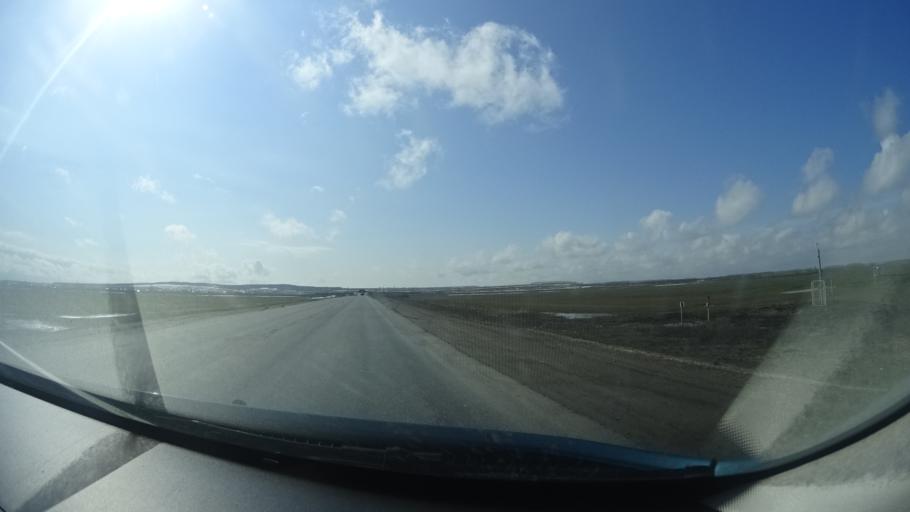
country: RU
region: Bashkortostan
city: Mikhaylovka
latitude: 54.8887
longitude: 55.7188
